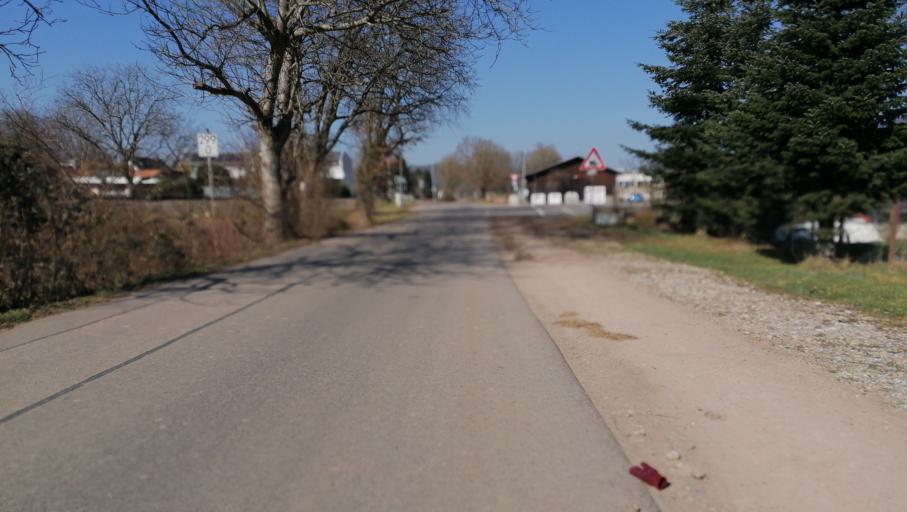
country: CH
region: Aargau
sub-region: Bezirk Rheinfelden
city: Mumpf
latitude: 47.5653
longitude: 7.9174
